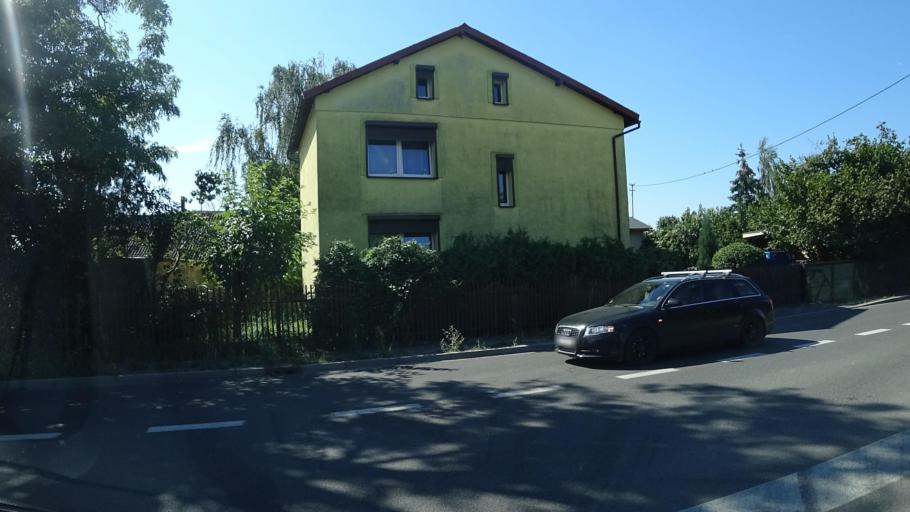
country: PL
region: Greater Poland Voivodeship
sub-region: Powiat koninski
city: Slesin
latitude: 52.3726
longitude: 18.3227
